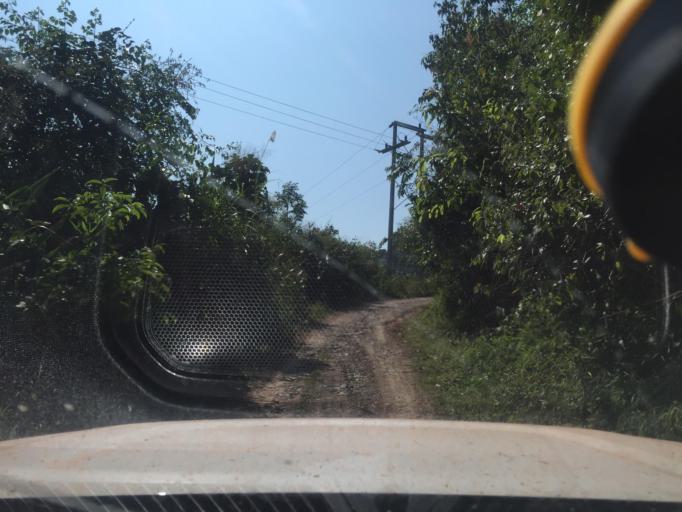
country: LA
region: Phongsali
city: Phongsali
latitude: 21.6566
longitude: 102.4165
